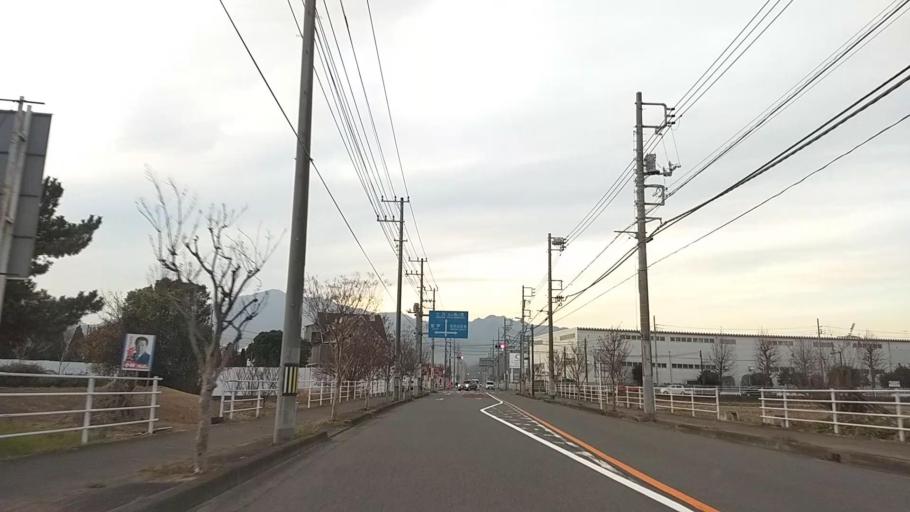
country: JP
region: Kanagawa
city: Atsugi
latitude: 35.4305
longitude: 139.3309
